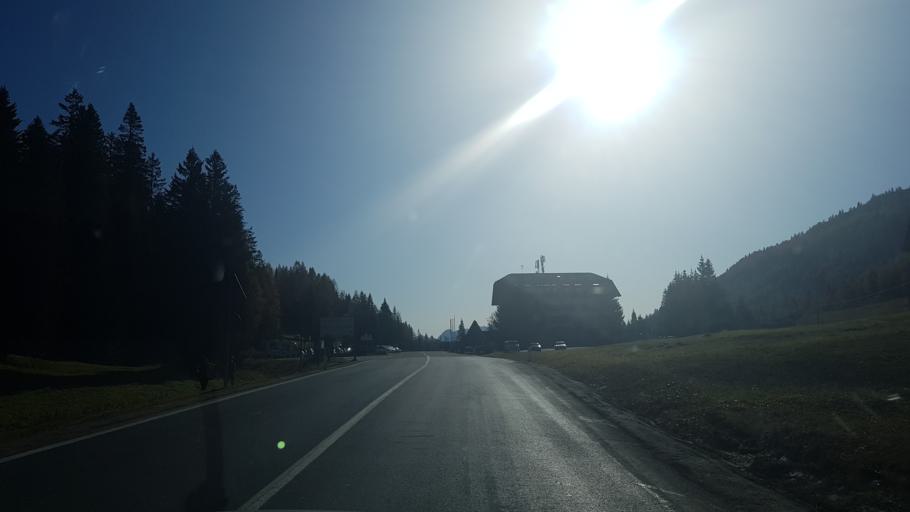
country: IT
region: Trentino-Alto Adige
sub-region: Bolzano
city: Sesto
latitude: 46.6571
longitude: 12.4180
